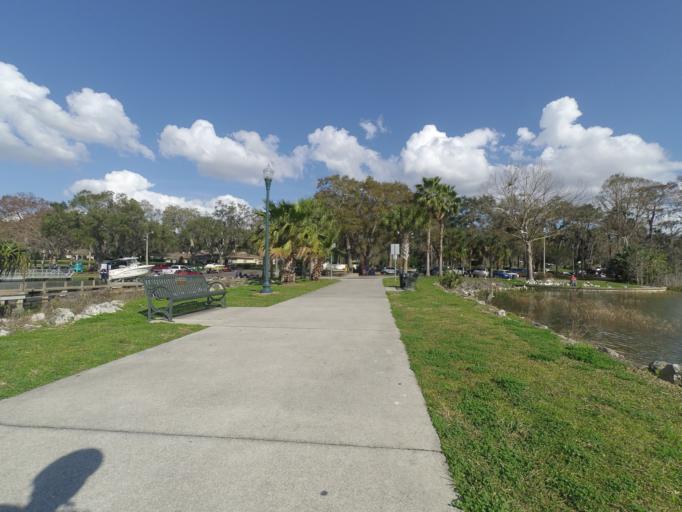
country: US
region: Florida
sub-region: Lake County
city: Mount Dora
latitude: 28.7948
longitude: -81.6433
